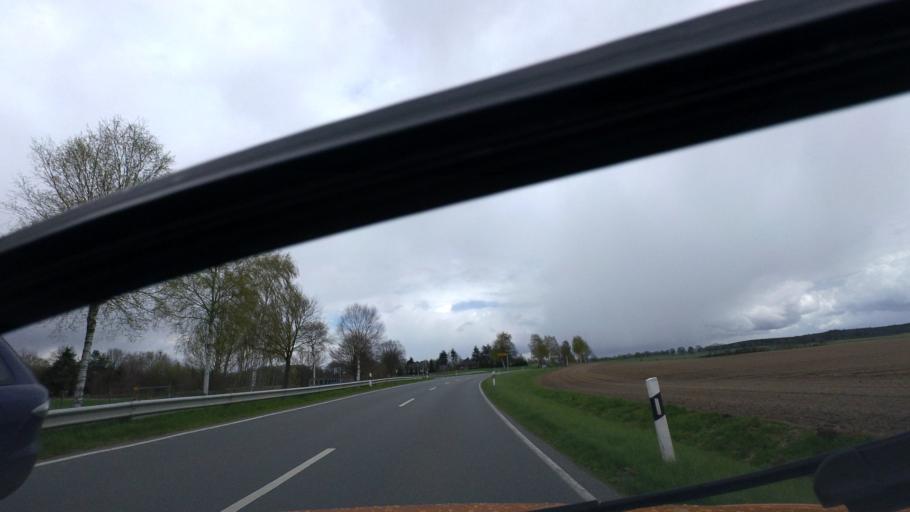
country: DE
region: Lower Saxony
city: Bispingen
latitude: 53.1366
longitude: 10.0217
